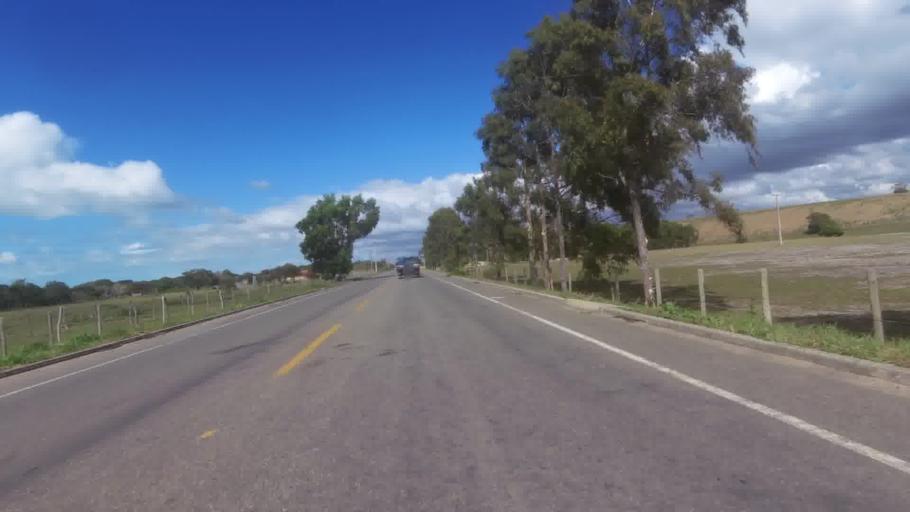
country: BR
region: Espirito Santo
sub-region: Marataizes
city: Marataizes
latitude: -21.1950
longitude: -40.9432
